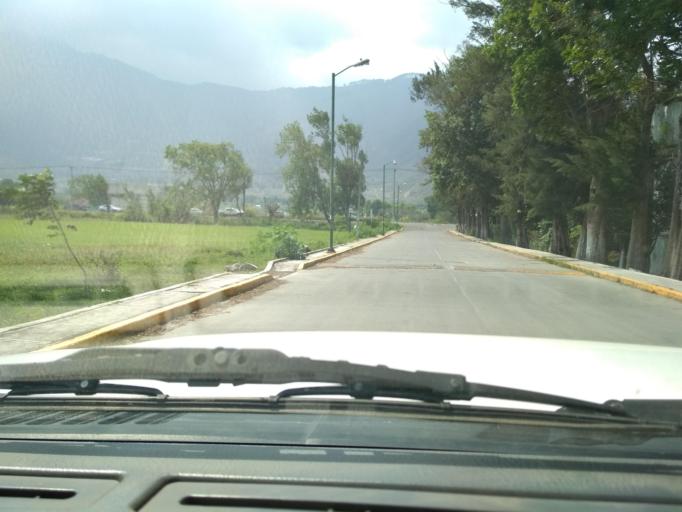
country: MX
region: Veracruz
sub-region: Acultzingo
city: Acatla
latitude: 18.7669
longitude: -97.2198
